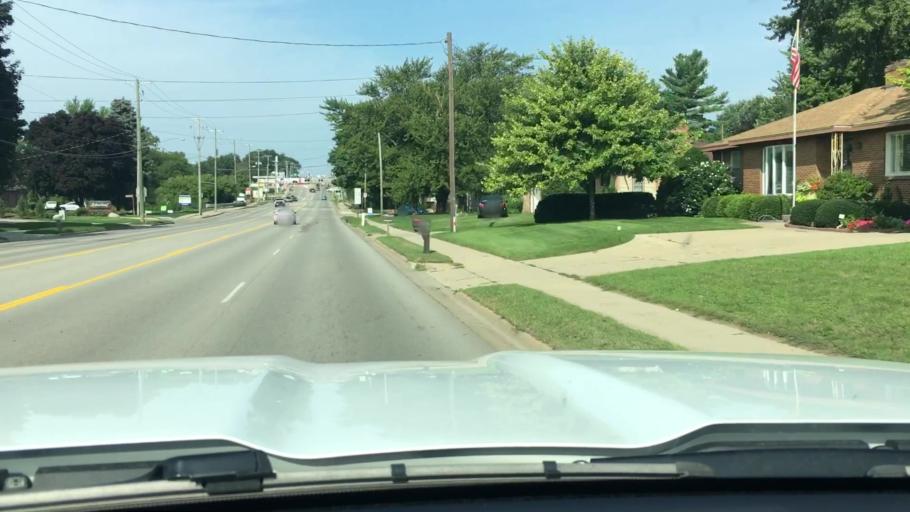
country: US
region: Michigan
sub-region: Kent County
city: Cutlerville
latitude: 42.8409
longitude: -85.6705
